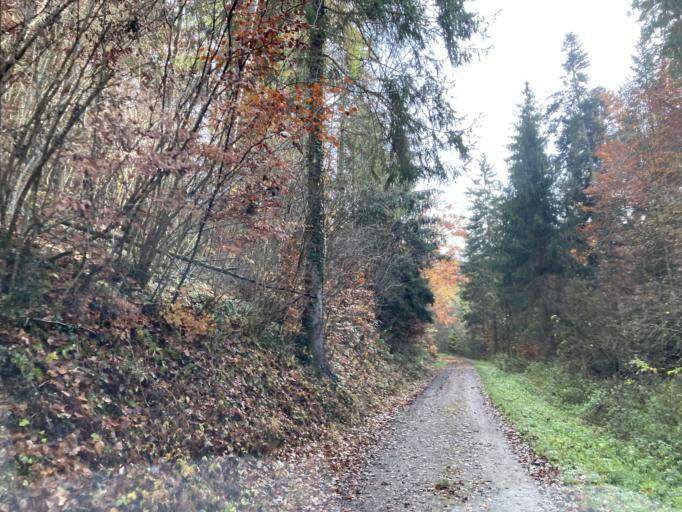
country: DE
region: Baden-Wuerttemberg
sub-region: Regierungsbezirk Stuttgart
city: Bondorf
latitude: 48.4785
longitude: 8.8285
